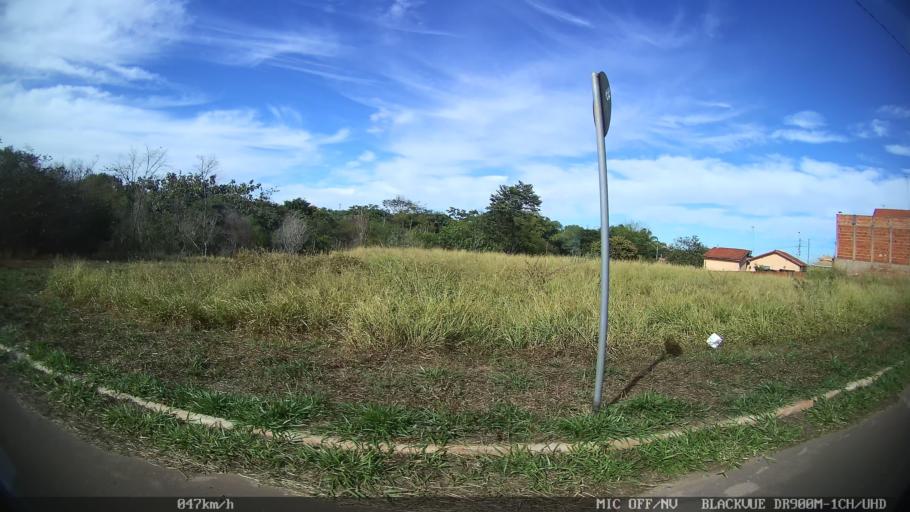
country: BR
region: Sao Paulo
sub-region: Catanduva
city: Catanduva
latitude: -21.1205
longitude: -48.9741
